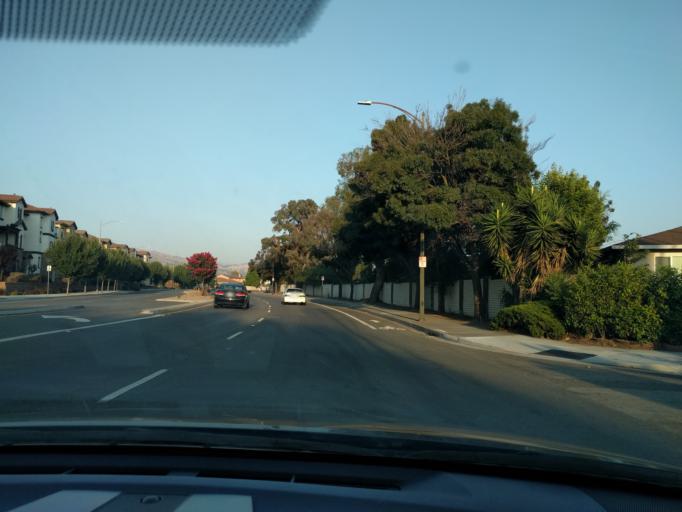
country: US
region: California
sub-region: Santa Clara County
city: Alum Rock
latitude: 37.3791
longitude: -121.8662
